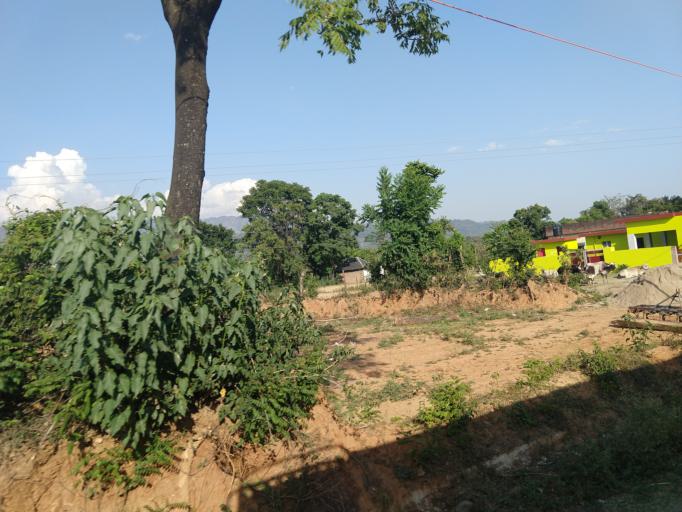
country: IN
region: Himachal Pradesh
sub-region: Chamba
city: Chowari
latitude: 32.3661
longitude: 75.9215
